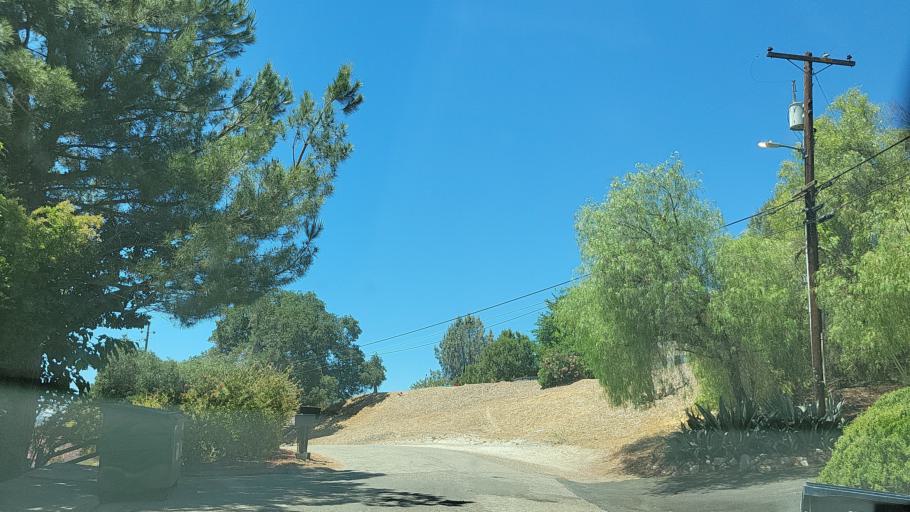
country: US
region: California
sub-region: San Luis Obispo County
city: Atascadero
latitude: 35.4665
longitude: -120.6469
